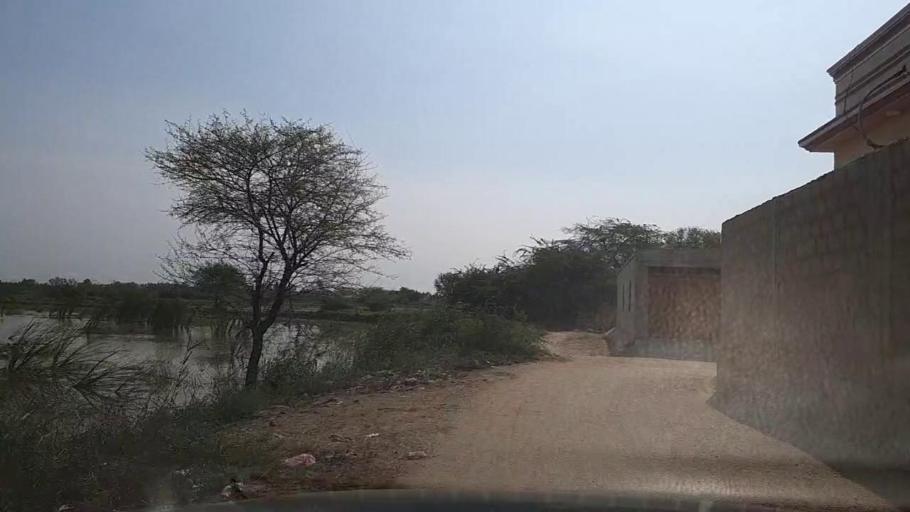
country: PK
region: Sindh
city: Thatta
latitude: 24.5661
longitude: 67.8922
